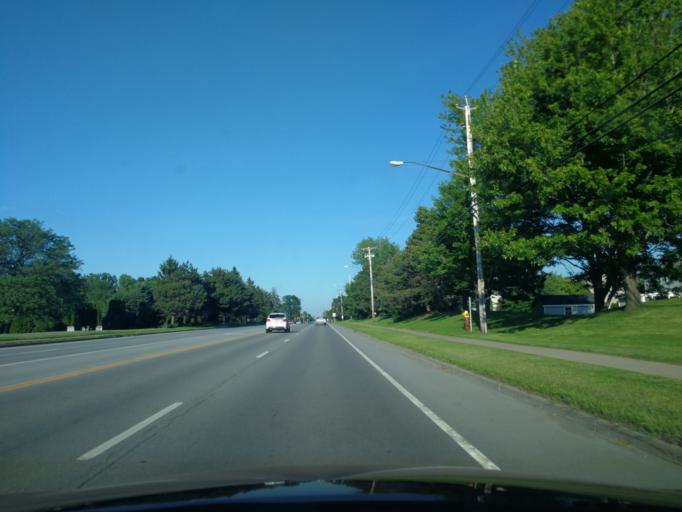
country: US
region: New York
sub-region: Monroe County
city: Greece
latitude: 43.2530
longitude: -77.7063
